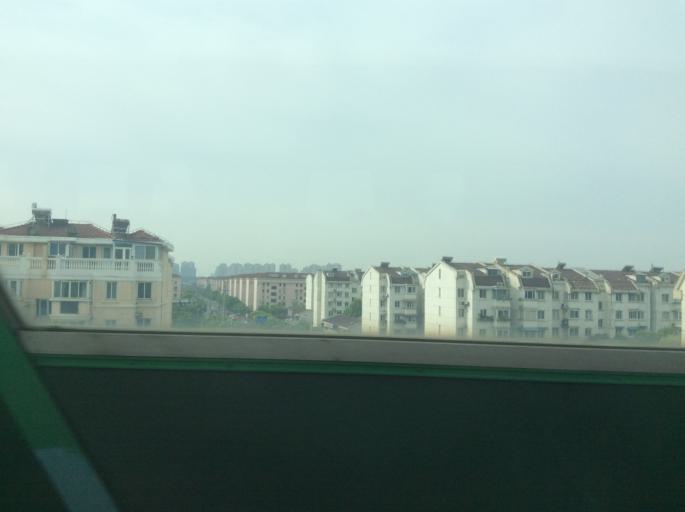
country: CN
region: Shanghai Shi
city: Changqiao
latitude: 31.1501
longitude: 121.4897
